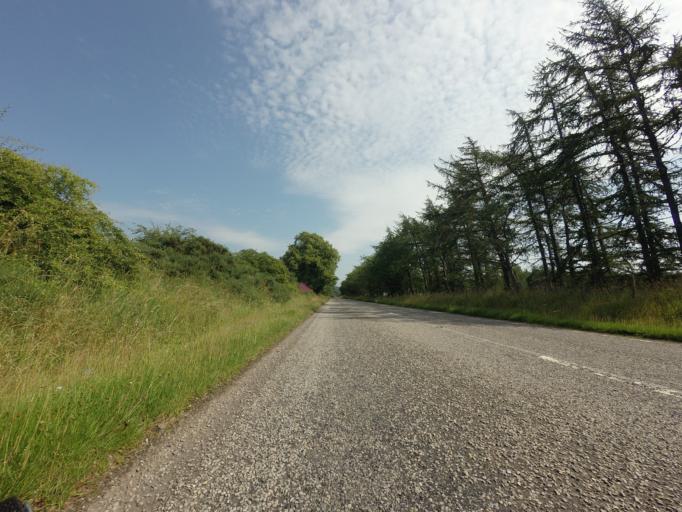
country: GB
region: Scotland
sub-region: Highland
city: Alness
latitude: 57.9151
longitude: -4.3858
